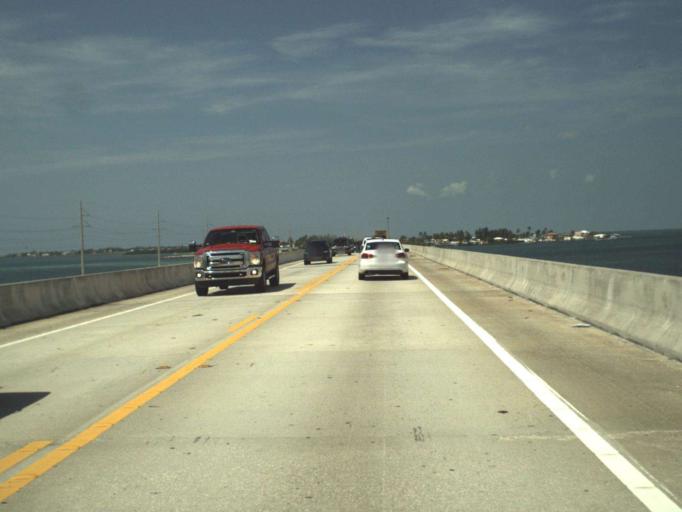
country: US
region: Florida
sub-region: Monroe County
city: Marathon
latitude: 24.7932
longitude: -80.8786
